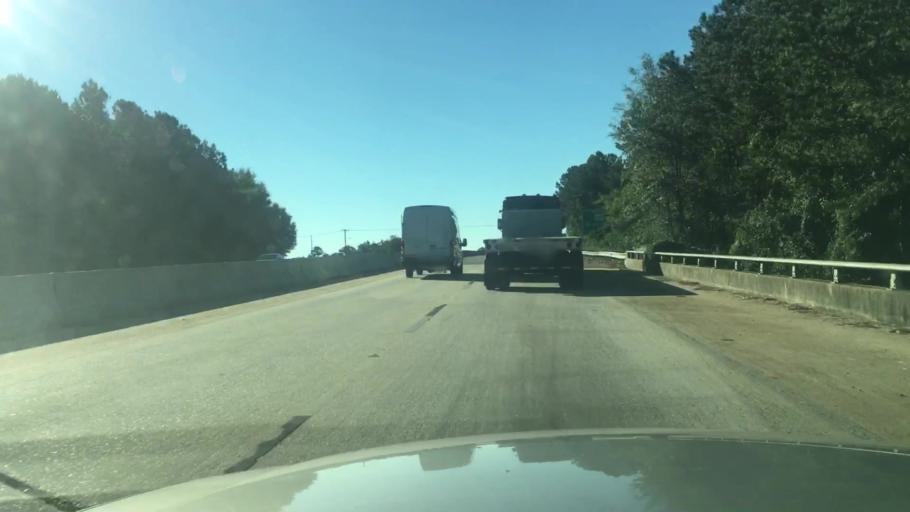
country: US
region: North Carolina
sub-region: Cumberland County
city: Fayetteville
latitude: 35.0462
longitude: -78.9405
